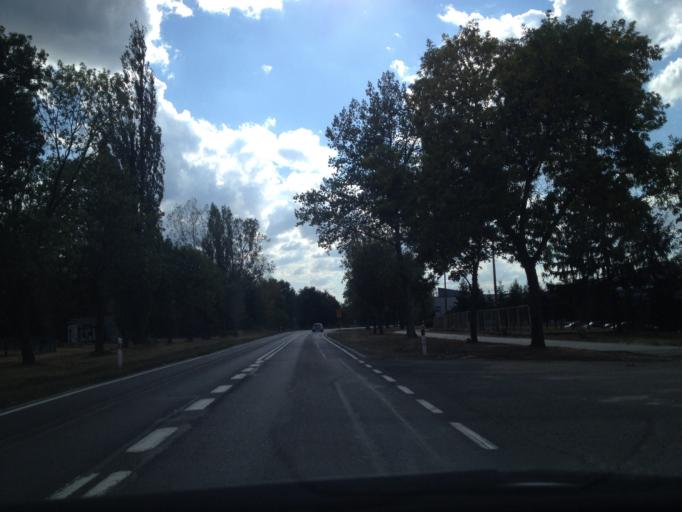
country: PL
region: Lubusz
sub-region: Powiat zarski
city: Zary
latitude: 51.6327
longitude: 15.1053
